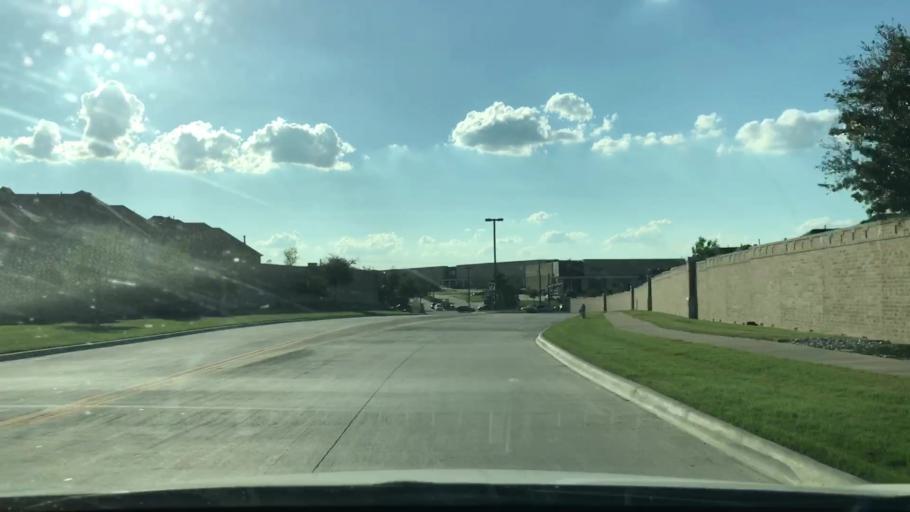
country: US
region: Texas
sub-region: Dallas County
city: Coppell
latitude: 32.8995
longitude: -96.9889
